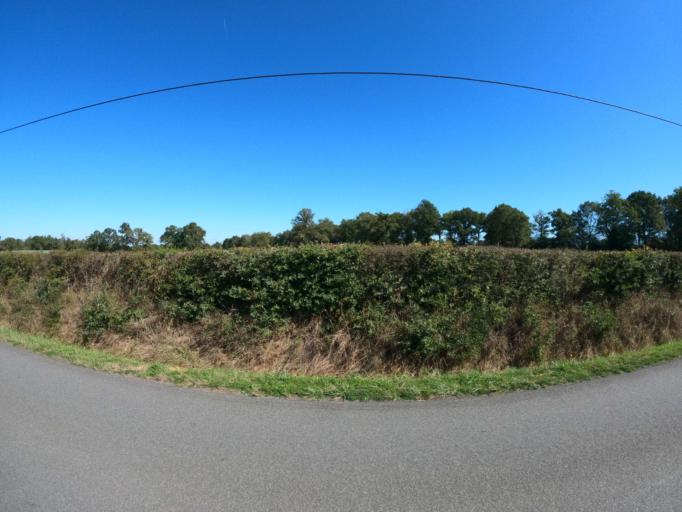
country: FR
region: Limousin
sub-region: Departement de la Haute-Vienne
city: Le Dorat
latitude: 46.2679
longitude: 1.0278
